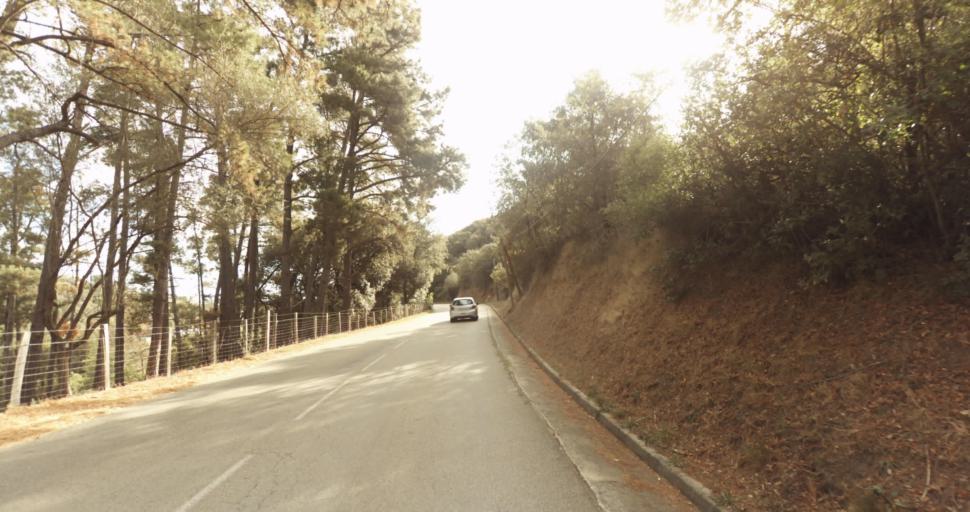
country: FR
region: Corsica
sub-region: Departement de la Corse-du-Sud
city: Ajaccio
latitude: 41.9301
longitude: 8.7136
